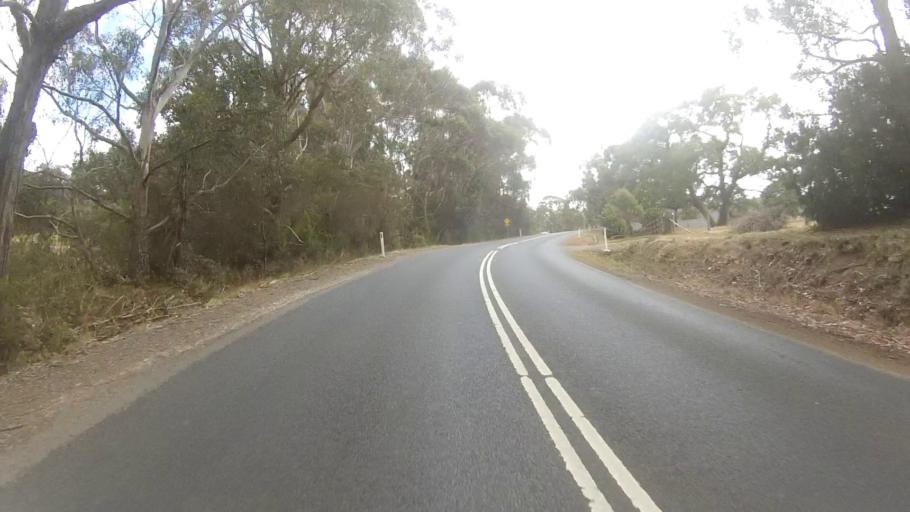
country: AU
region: Tasmania
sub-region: Kingborough
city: Margate
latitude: -43.0110
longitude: 147.2432
